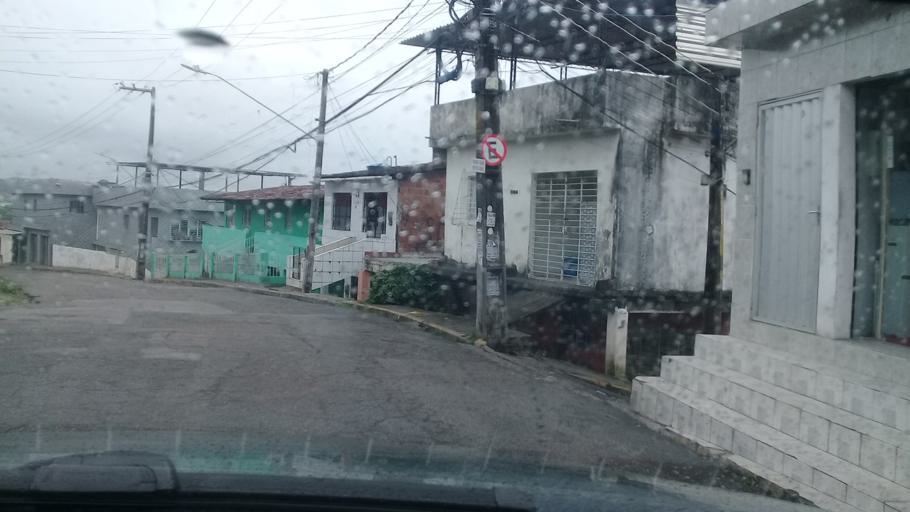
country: BR
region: Pernambuco
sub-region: Jaboatao Dos Guararapes
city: Jaboatao dos Guararapes
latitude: -8.0845
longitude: -34.9762
